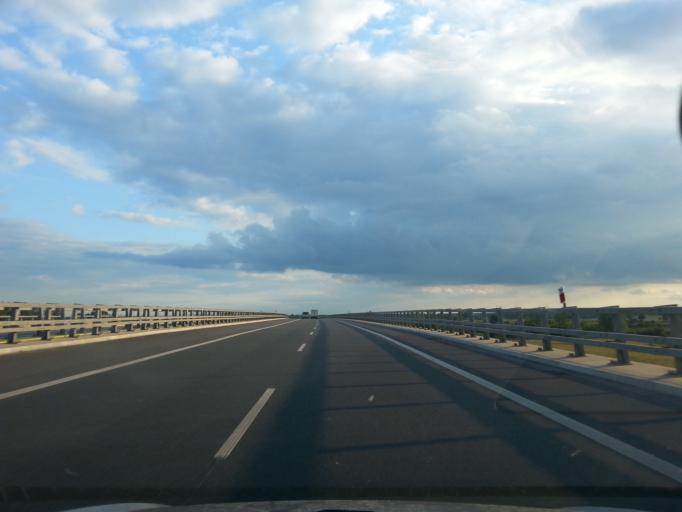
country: PL
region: Lodz Voivodeship
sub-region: Powiat sieradzki
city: Sieradz
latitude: 51.5861
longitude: 18.8052
